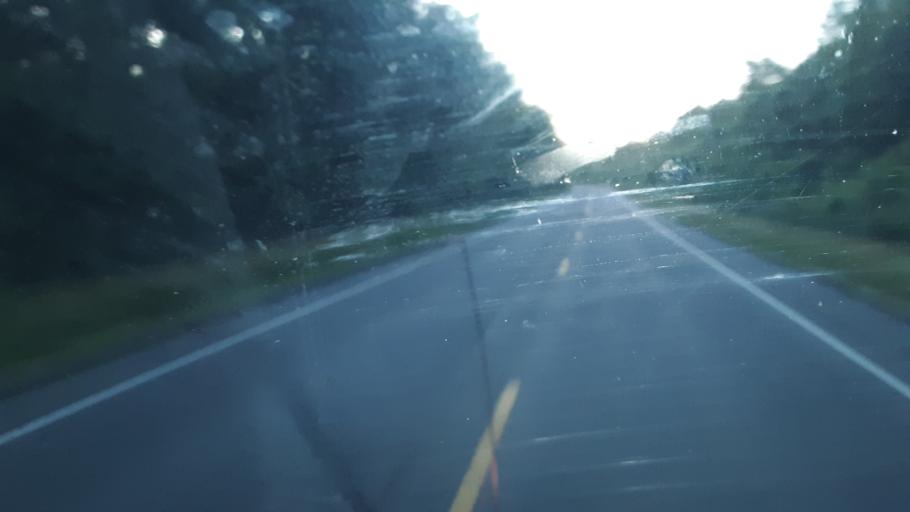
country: US
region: New York
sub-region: Schenectady County
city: East Glenville
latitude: 42.9767
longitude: -73.9629
